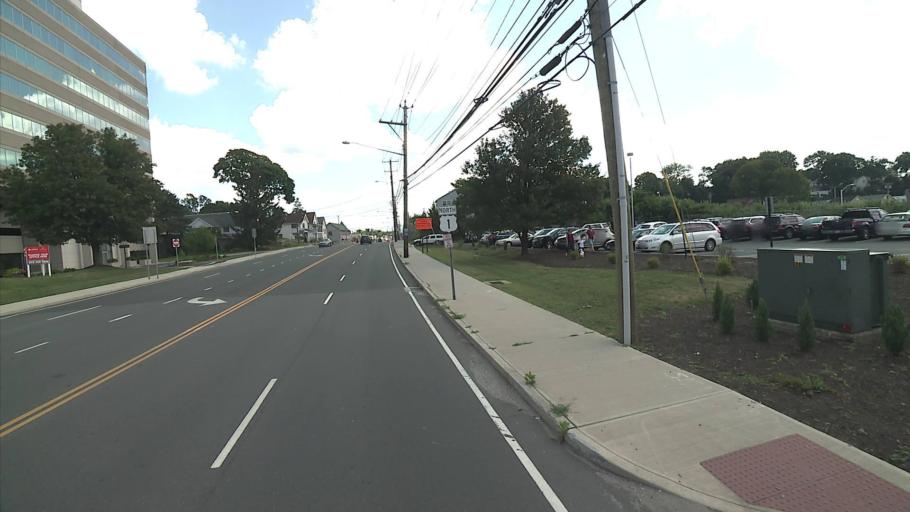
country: US
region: Connecticut
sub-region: Fairfield County
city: Norwalk
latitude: 41.1040
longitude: -73.4323
